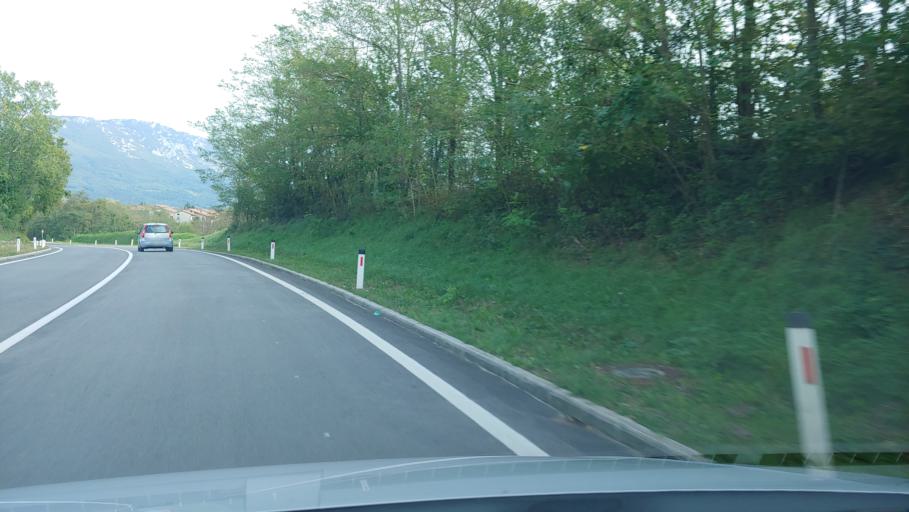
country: SI
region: Ajdovscina
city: Lokavec
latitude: 45.8878
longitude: 13.8559
